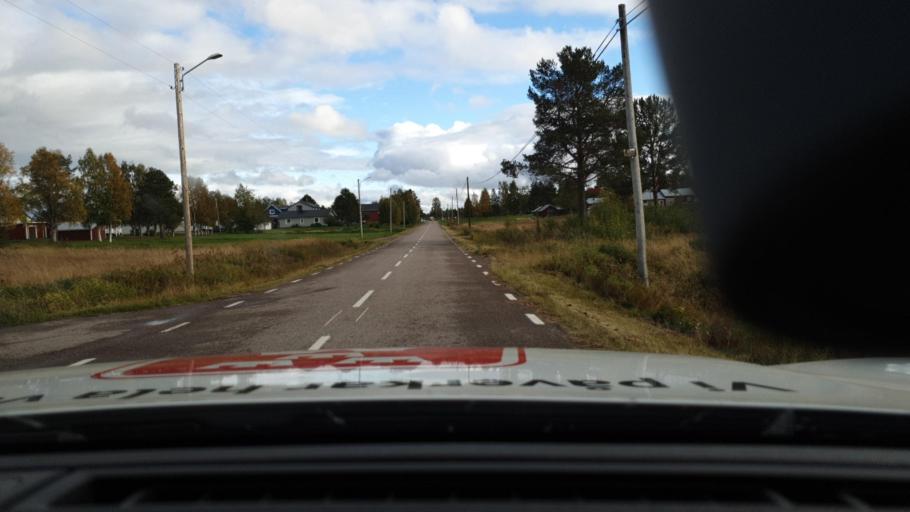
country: SE
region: Norrbotten
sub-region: Overkalix Kommun
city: OEverkalix
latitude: 67.0063
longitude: 22.4887
